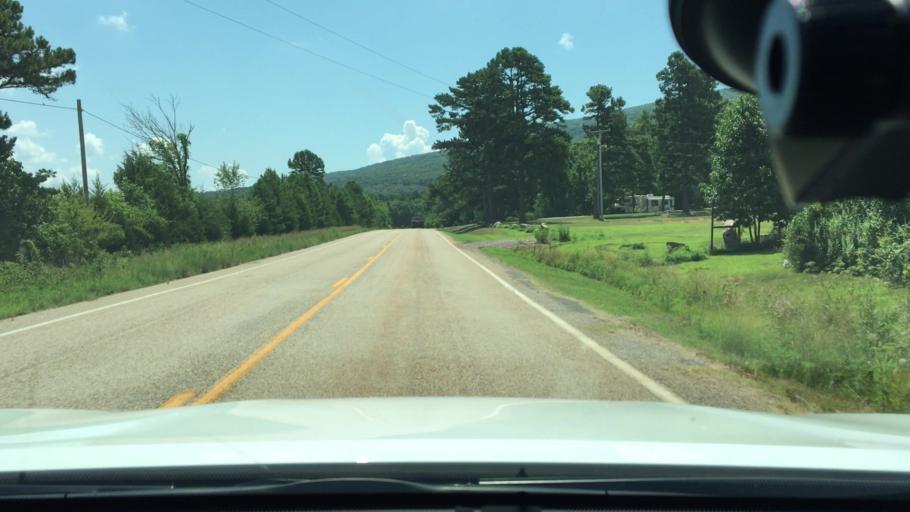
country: US
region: Arkansas
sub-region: Logan County
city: Paris
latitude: 35.1923
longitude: -93.6271
